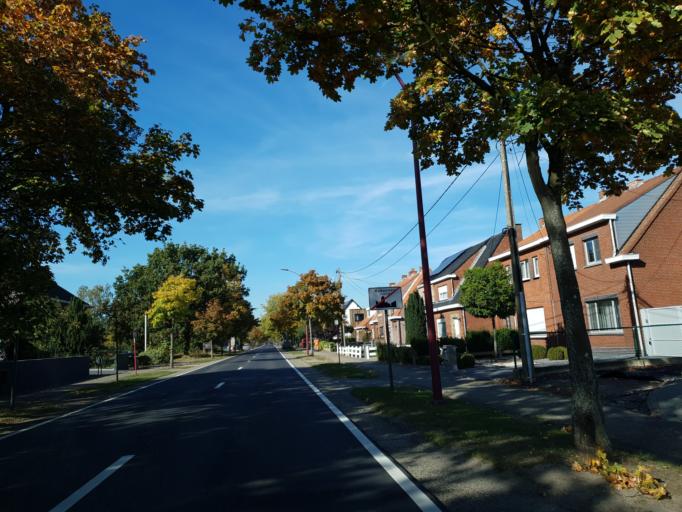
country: BE
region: Flanders
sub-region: Provincie Antwerpen
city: Stabroek
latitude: 51.3155
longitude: 4.3946
